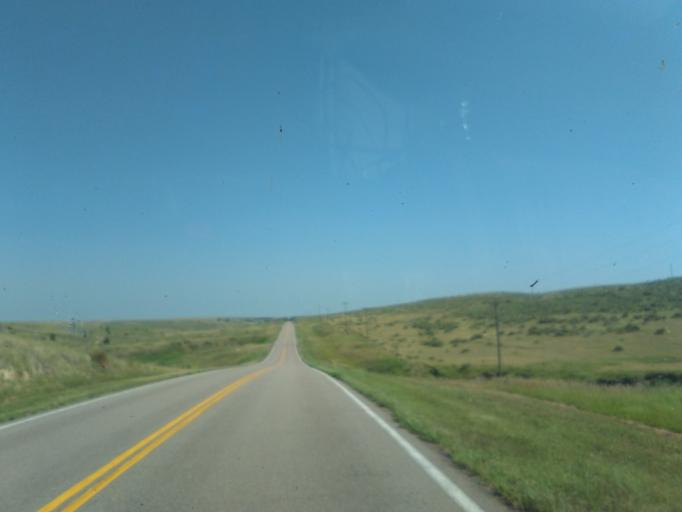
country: US
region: Nebraska
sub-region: Dundy County
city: Benkelman
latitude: 39.8708
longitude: -101.5411
